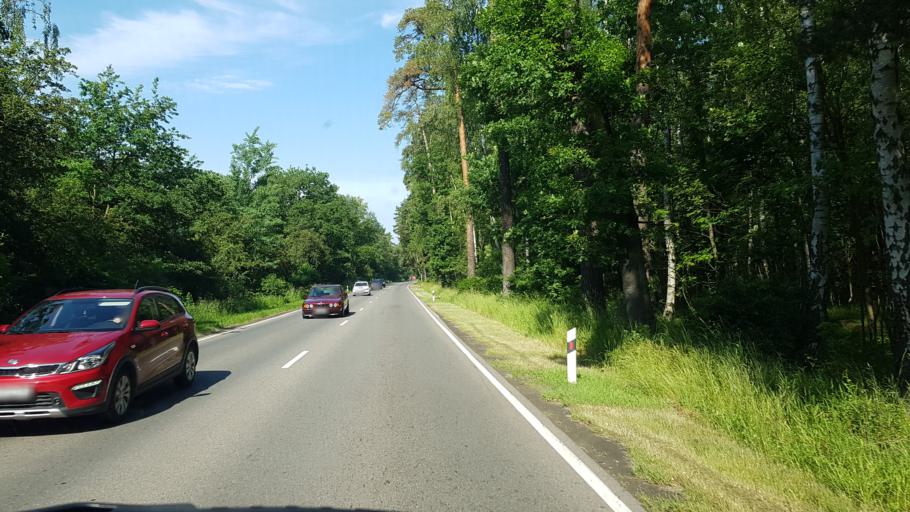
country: RU
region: Kaliningrad
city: Vzmorye
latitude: 54.7047
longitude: 20.2930
